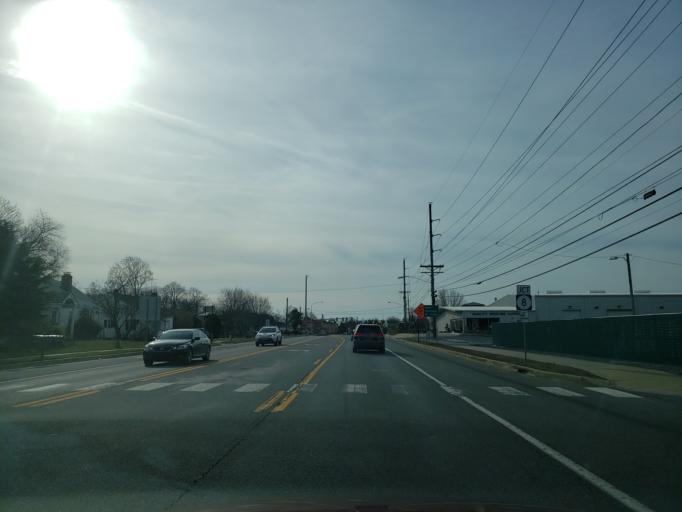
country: US
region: Delaware
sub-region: Kent County
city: Dover
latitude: 39.1609
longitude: -75.5436
